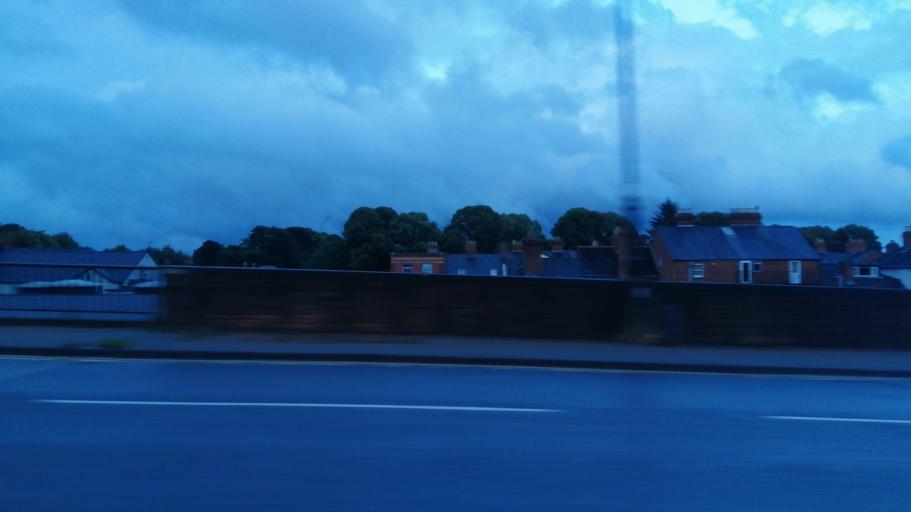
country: GB
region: England
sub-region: Herefordshire
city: Hereford
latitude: 52.0515
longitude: -2.7197
